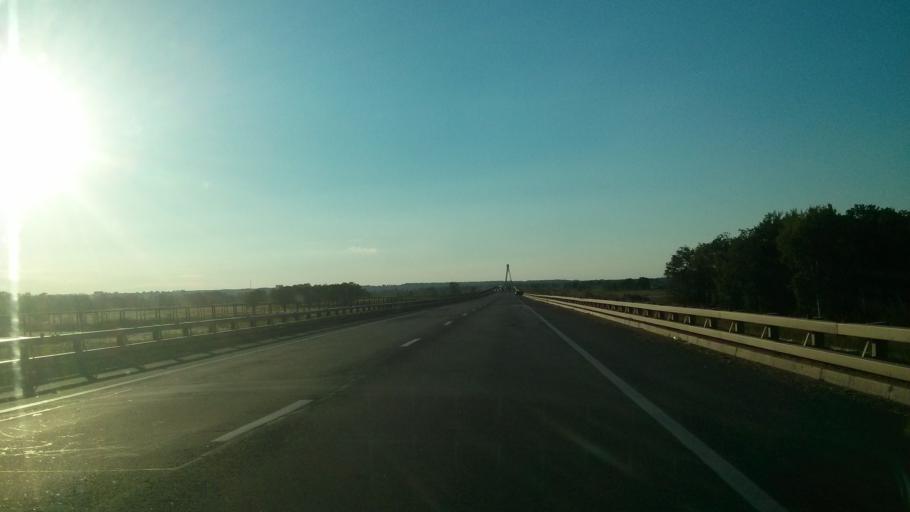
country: RU
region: Vladimir
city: Murom
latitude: 55.6014
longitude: 42.0991
